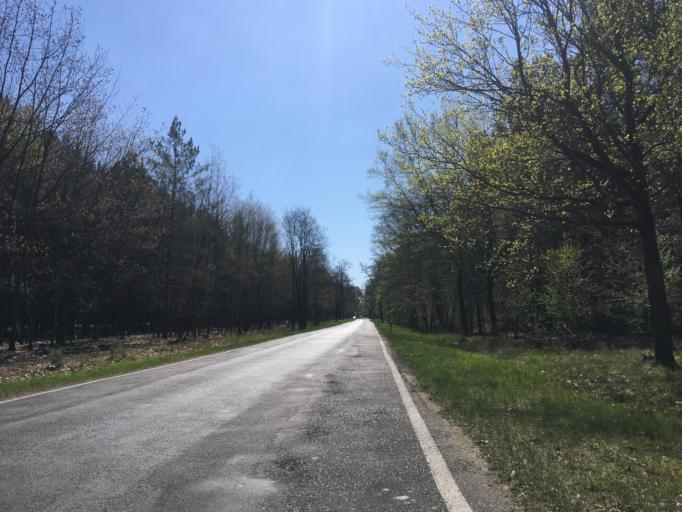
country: DE
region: Brandenburg
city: Bernau bei Berlin
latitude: 52.7112
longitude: 13.5811
